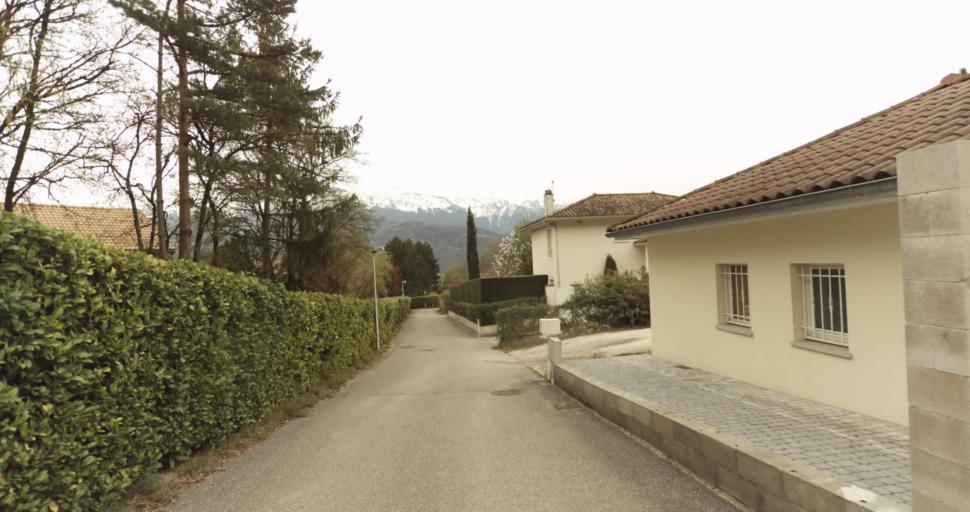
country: FR
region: Rhone-Alpes
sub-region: Departement de l'Isere
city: Biviers
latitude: 45.2369
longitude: 5.8151
